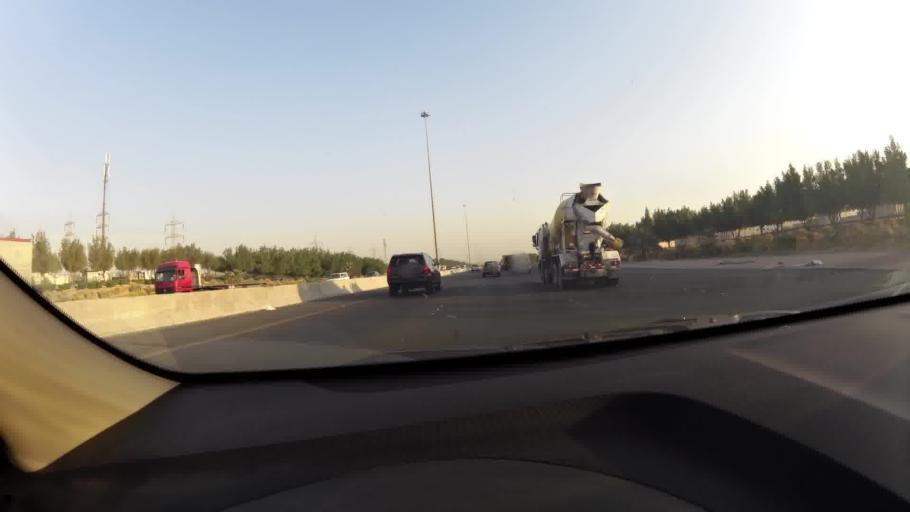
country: KW
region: Al Ahmadi
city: Ar Riqqah
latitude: 29.1573
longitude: 48.0779
